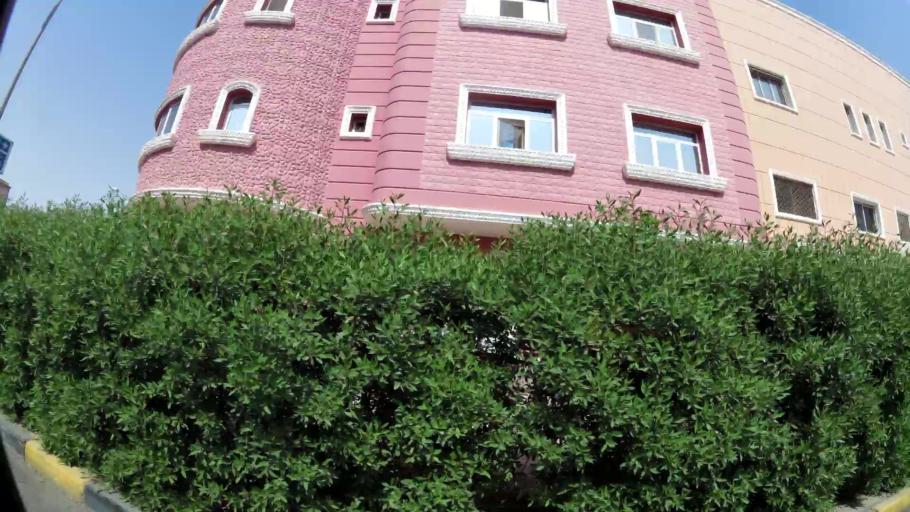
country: KW
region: Muhafazat al Jahra'
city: Al Jahra'
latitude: 29.3240
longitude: 47.6690
